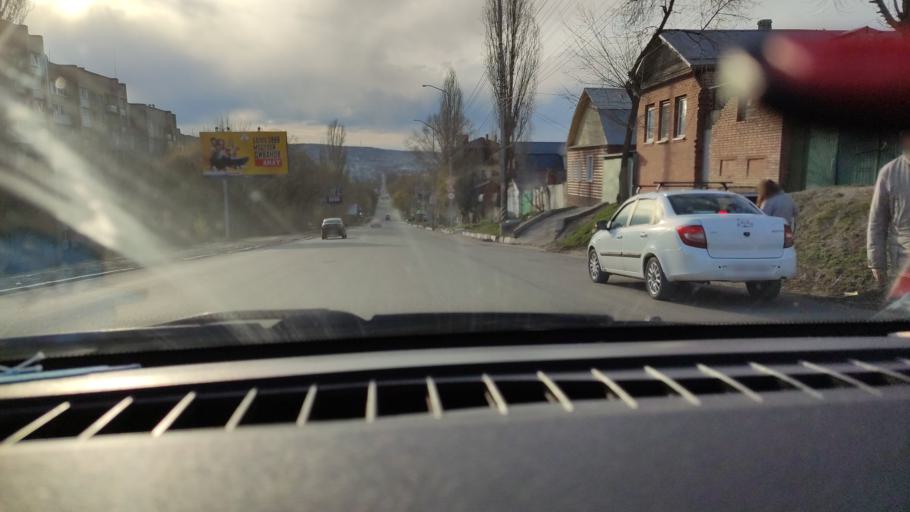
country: RU
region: Saratov
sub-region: Saratovskiy Rayon
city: Saratov
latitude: 51.5413
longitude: 46.0447
